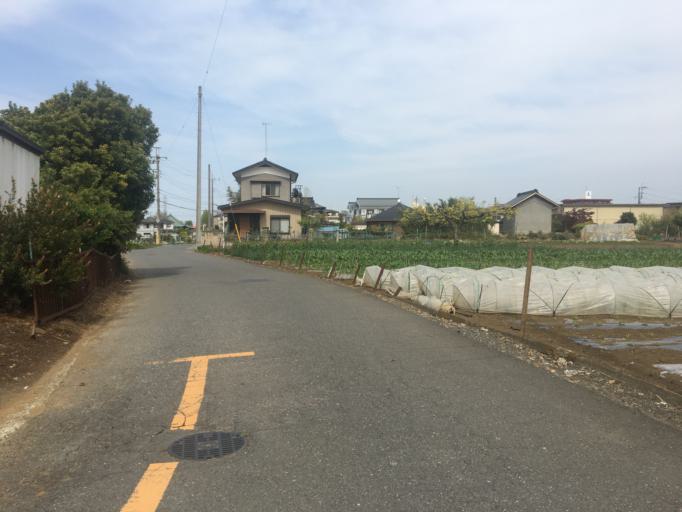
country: JP
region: Saitama
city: Shiki
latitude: 35.8130
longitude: 139.5497
